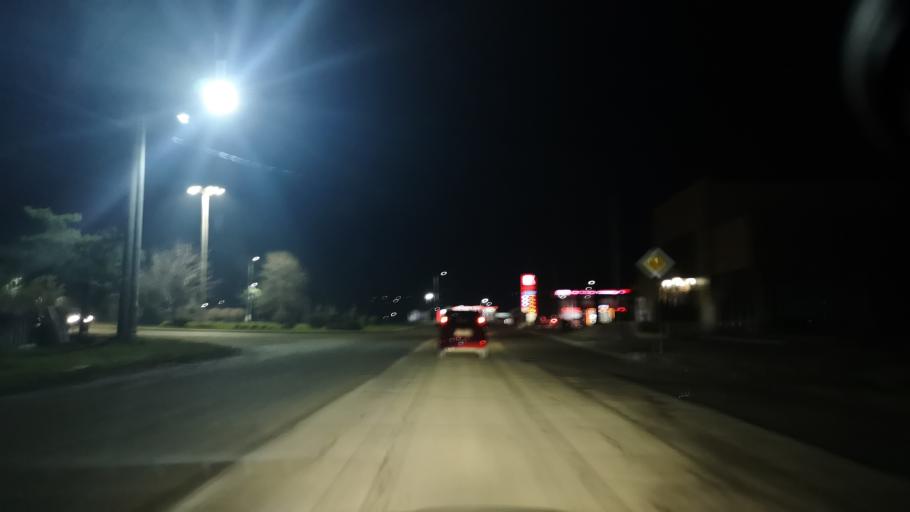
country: MD
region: Orhei
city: Orhei
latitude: 47.3710
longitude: 28.8166
